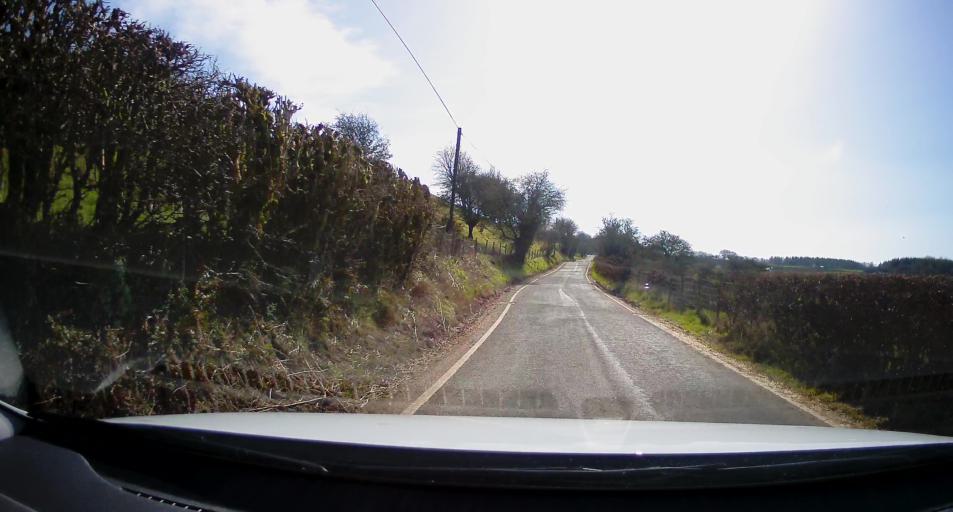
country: GB
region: Wales
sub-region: County of Ceredigion
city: Lledrod
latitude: 52.2803
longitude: -4.0618
